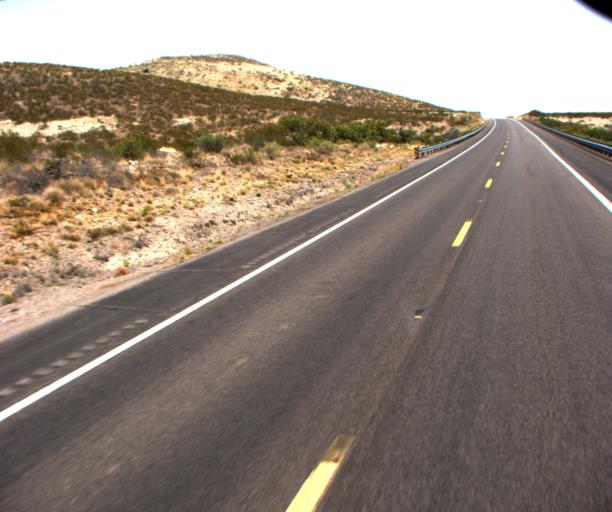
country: US
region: Arizona
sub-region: Greenlee County
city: Clifton
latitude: 32.7357
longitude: -109.1968
